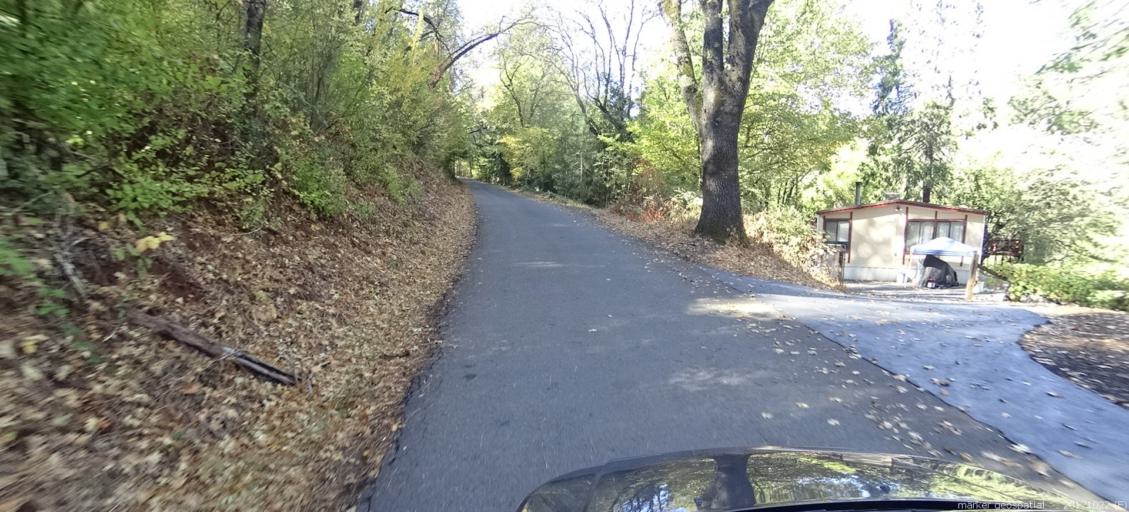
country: US
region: California
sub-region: Shasta County
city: Central Valley (historical)
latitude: 40.9436
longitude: -122.4247
